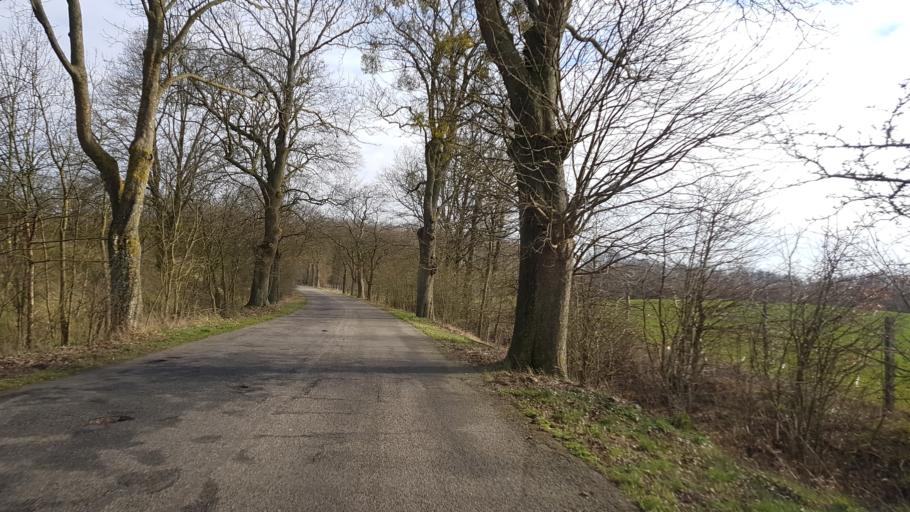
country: PL
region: West Pomeranian Voivodeship
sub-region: Powiat policki
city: Dobra
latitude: 53.5399
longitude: 14.3146
